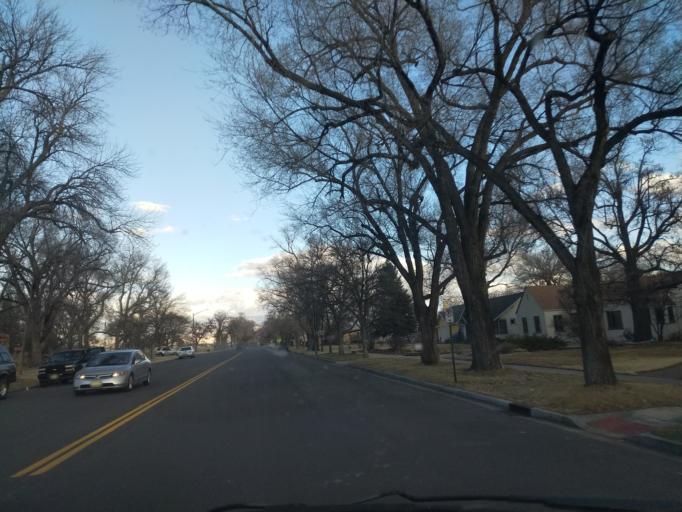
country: US
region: Colorado
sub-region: Mesa County
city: Grand Junction
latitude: 39.0734
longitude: -108.5507
